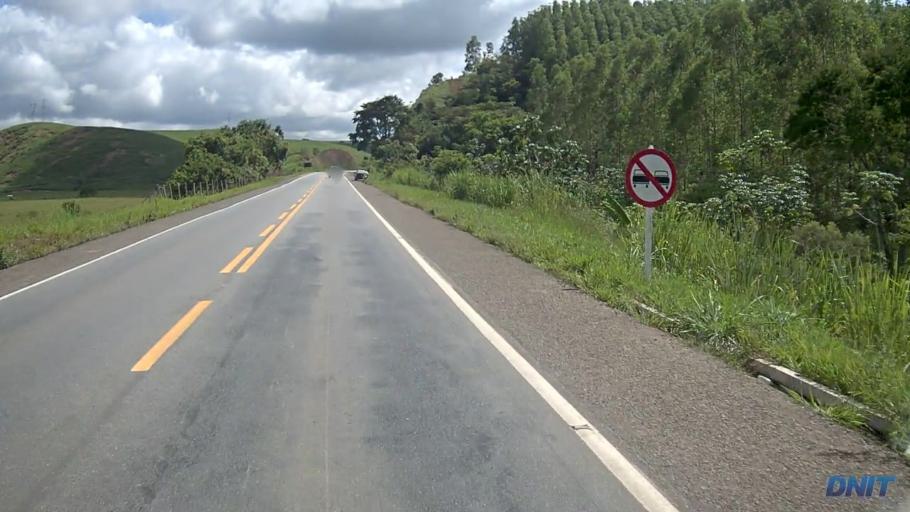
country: BR
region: Minas Gerais
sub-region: Belo Oriente
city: Belo Oriente
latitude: -19.1092
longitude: -42.2028
